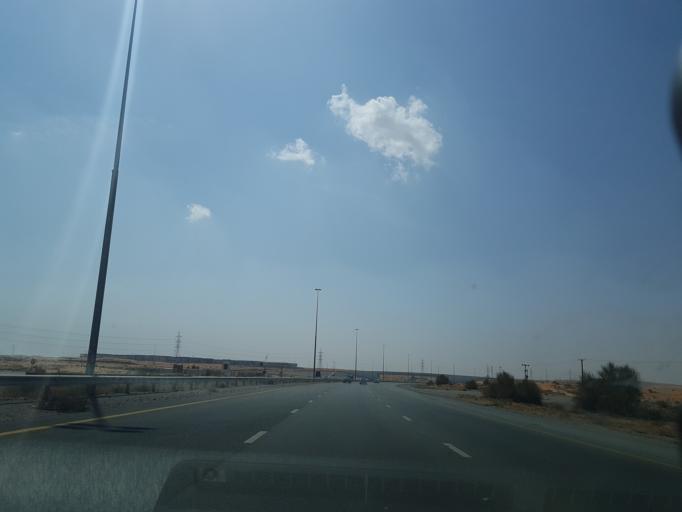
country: AE
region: Ra's al Khaymah
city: Ras al-Khaimah
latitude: 25.6763
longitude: 55.8829
